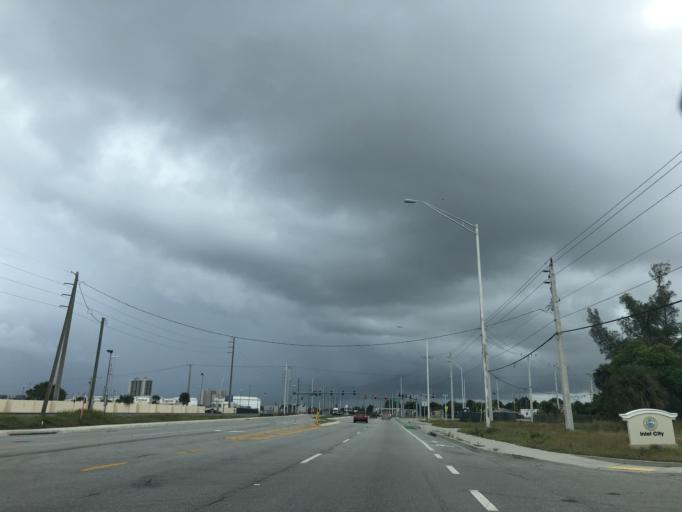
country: US
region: Florida
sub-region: Palm Beach County
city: Riviera Beach
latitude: 26.7709
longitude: -80.0622
